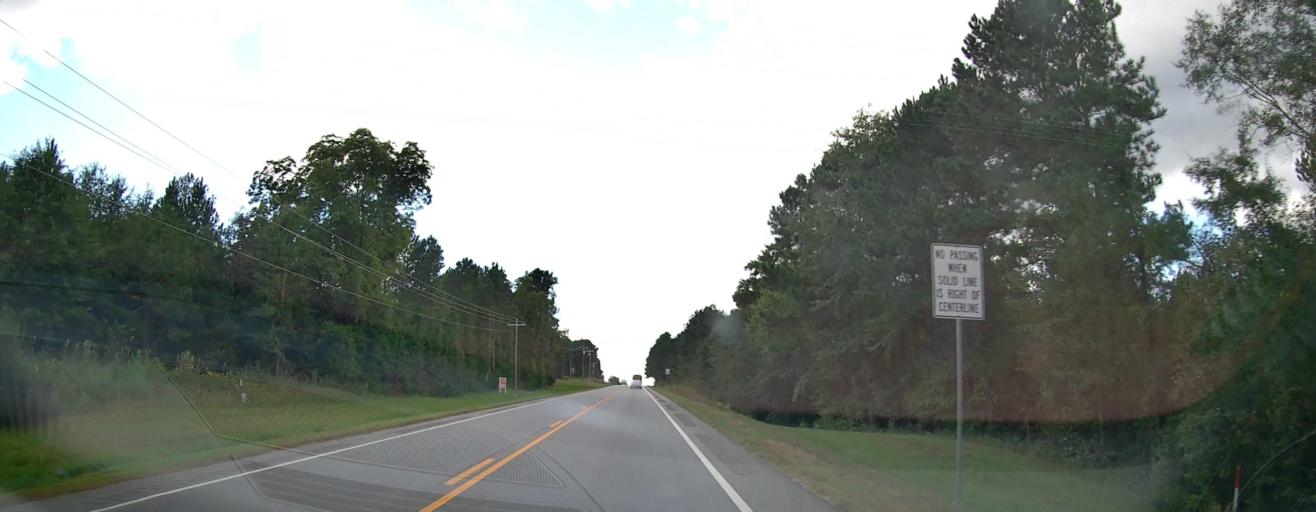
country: US
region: Georgia
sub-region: Baldwin County
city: Milledgeville
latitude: 33.0821
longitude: -83.2986
